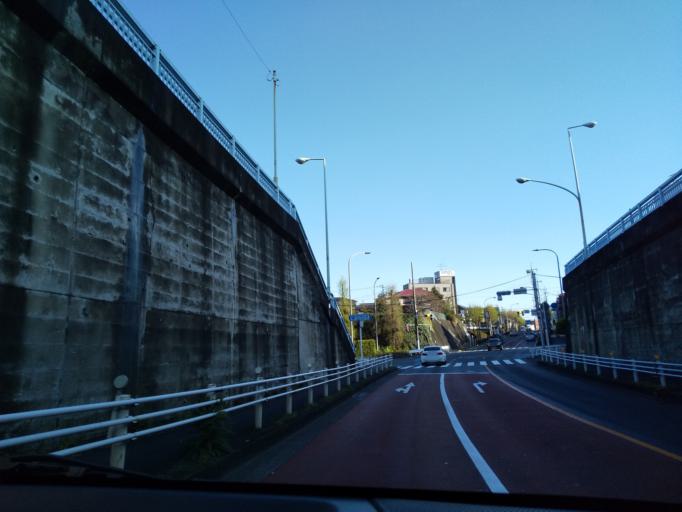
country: JP
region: Tokyo
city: Hachioji
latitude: 35.6629
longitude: 139.3569
